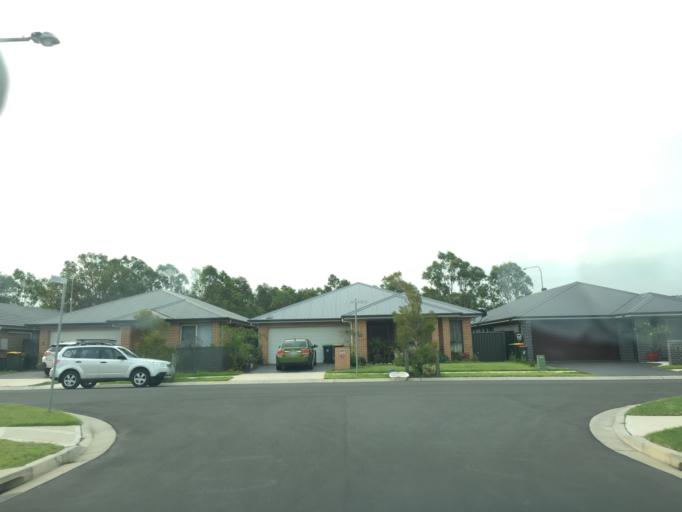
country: AU
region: New South Wales
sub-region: Campbelltown Municipality
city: Denham Court
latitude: -33.9805
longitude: 150.8042
